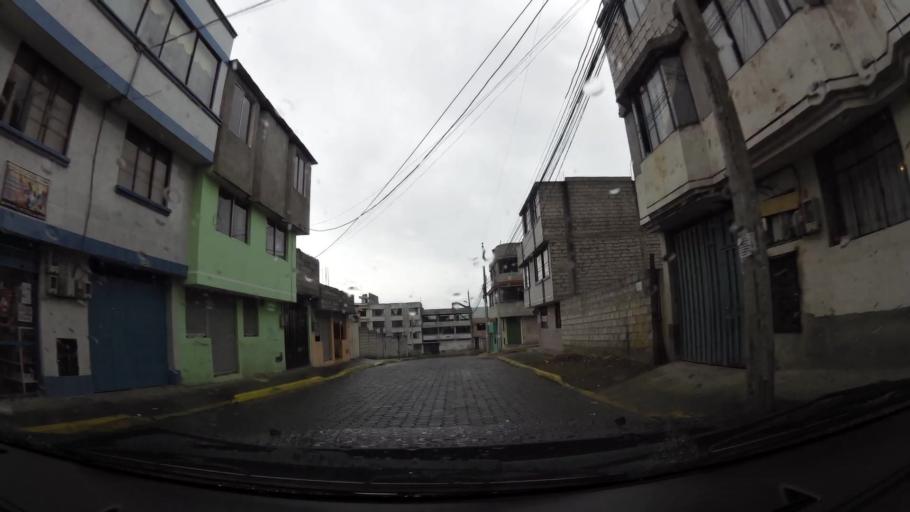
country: EC
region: Pichincha
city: Quito
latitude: -0.3225
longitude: -78.5536
